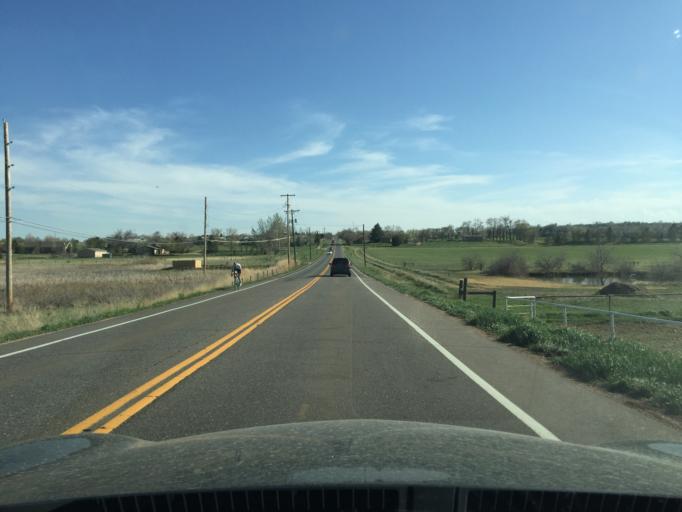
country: US
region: Colorado
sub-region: Boulder County
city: Niwot
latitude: 40.1129
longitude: -105.1313
